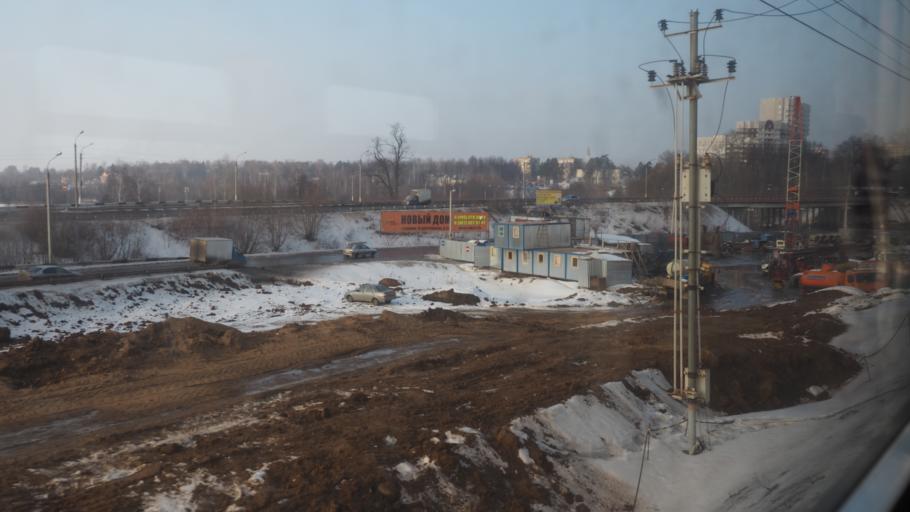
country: RU
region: Moskovskaya
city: Mamontovka
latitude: 56.0000
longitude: 37.8324
